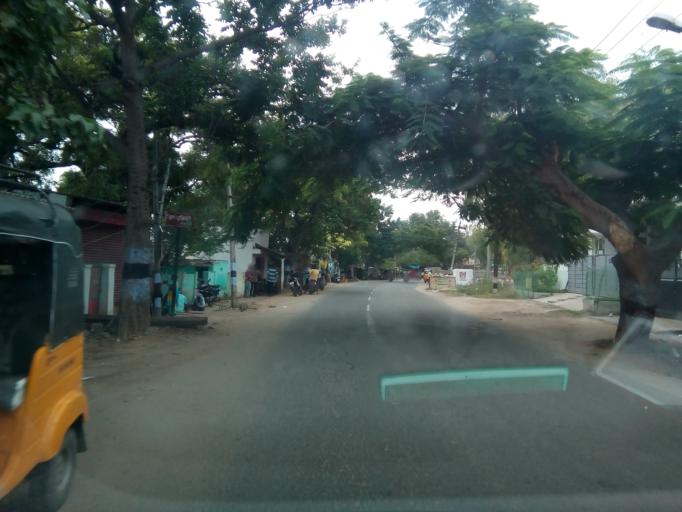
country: IN
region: Tamil Nadu
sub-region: Coimbatore
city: Coimbatore
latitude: 11.0057
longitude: 76.9401
